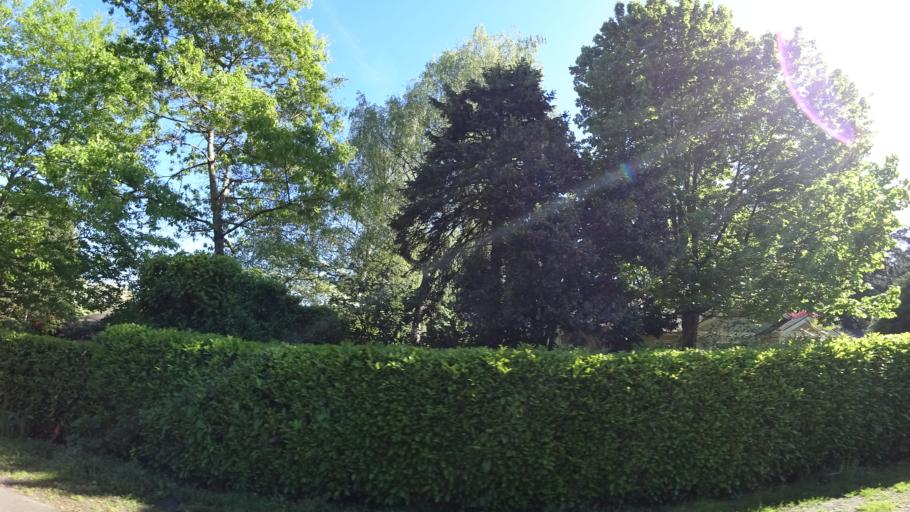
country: US
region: Oregon
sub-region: Washington County
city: Raleigh Hills
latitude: 45.4876
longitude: -122.7507
